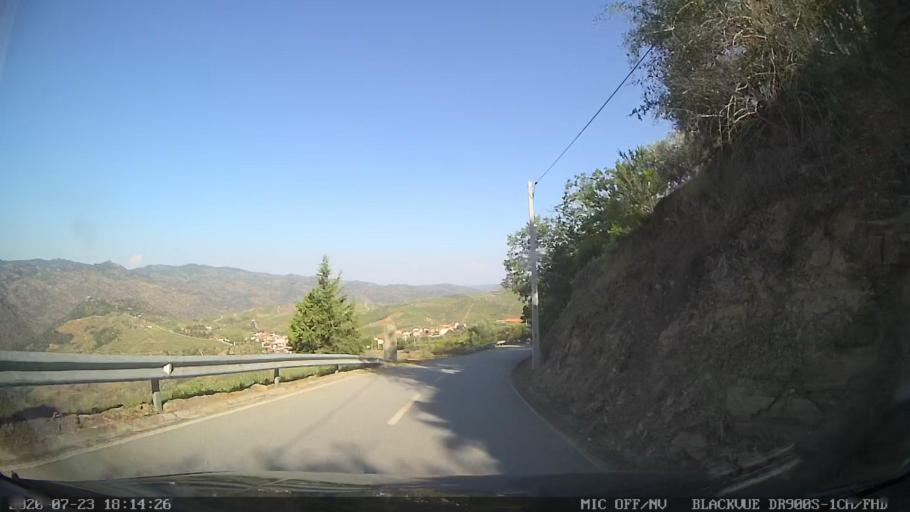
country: PT
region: Viseu
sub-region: Sao Joao da Pesqueira
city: Sao Joao da Pesqueira
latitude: 41.1869
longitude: -7.4226
